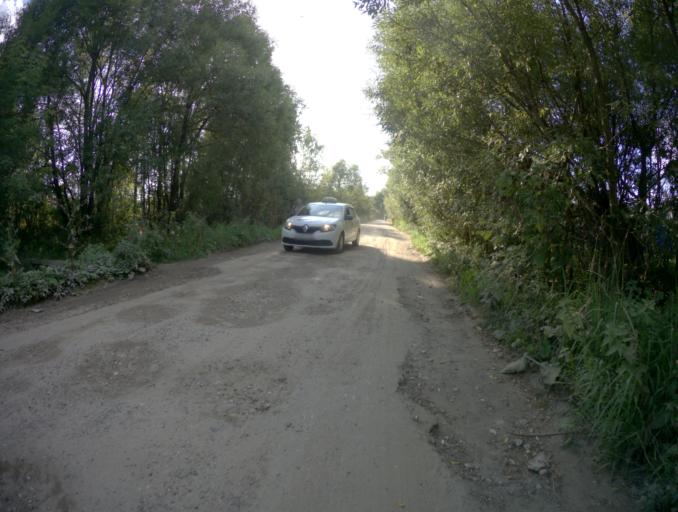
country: RU
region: Vladimir
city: Petushki
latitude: 55.9255
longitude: 39.4582
